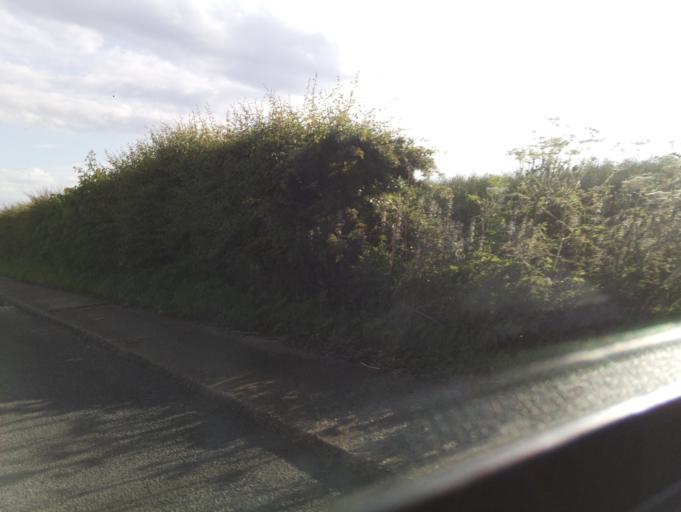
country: GB
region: England
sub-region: Lincolnshire
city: Navenby
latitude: 53.0650
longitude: -0.6365
